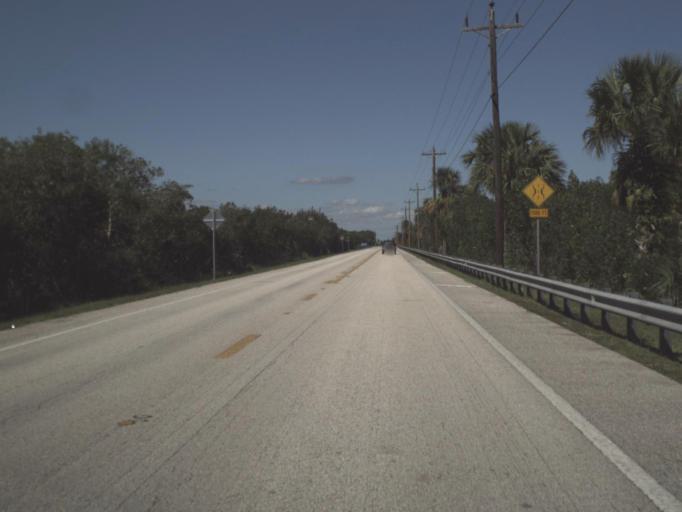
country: US
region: Florida
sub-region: Collier County
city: Marco
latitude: 25.9120
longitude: -81.3672
